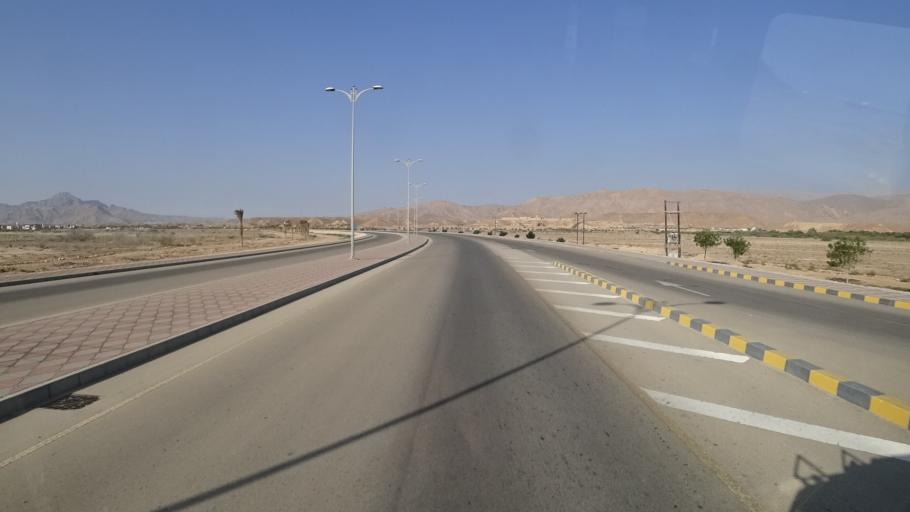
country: OM
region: Ash Sharqiyah
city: Sur
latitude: 22.5815
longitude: 59.4713
